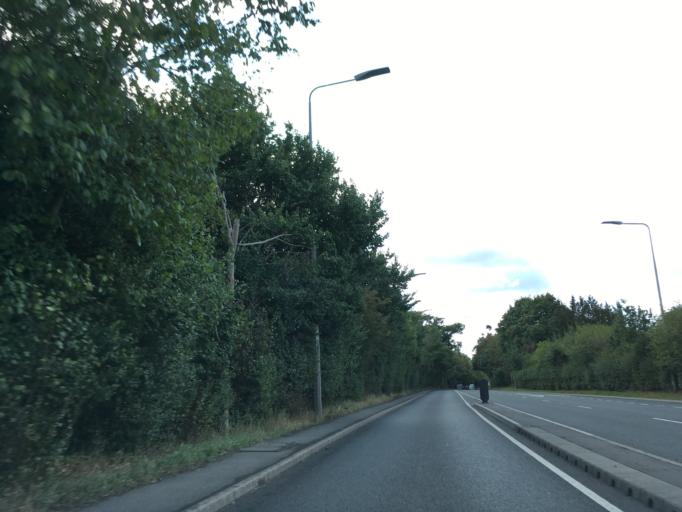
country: GB
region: England
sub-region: West Berkshire
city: Greenham
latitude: 51.3805
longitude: -1.3191
